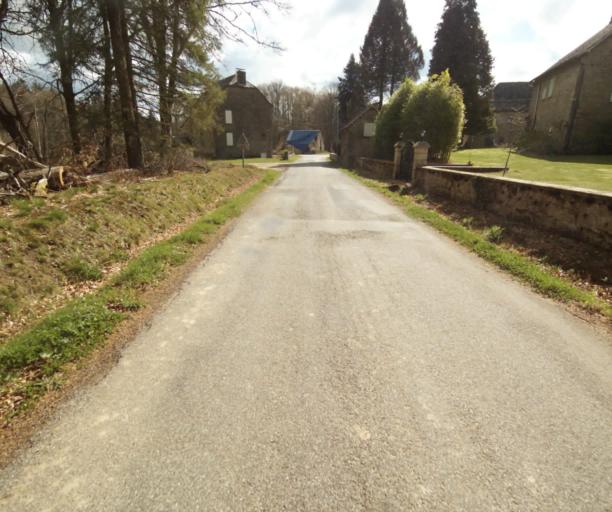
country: FR
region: Limousin
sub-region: Departement de la Correze
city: Correze
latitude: 45.2474
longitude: 1.9428
